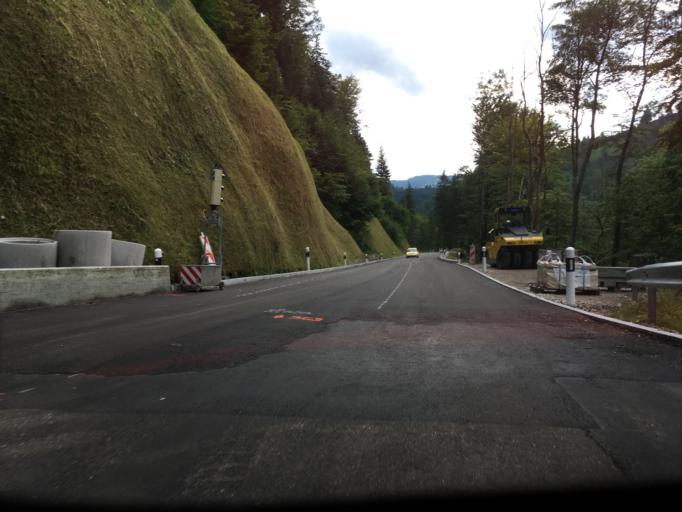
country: CH
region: Thurgau
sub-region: Muenchwilen District
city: Fischingen
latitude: 47.3578
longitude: 8.9666
